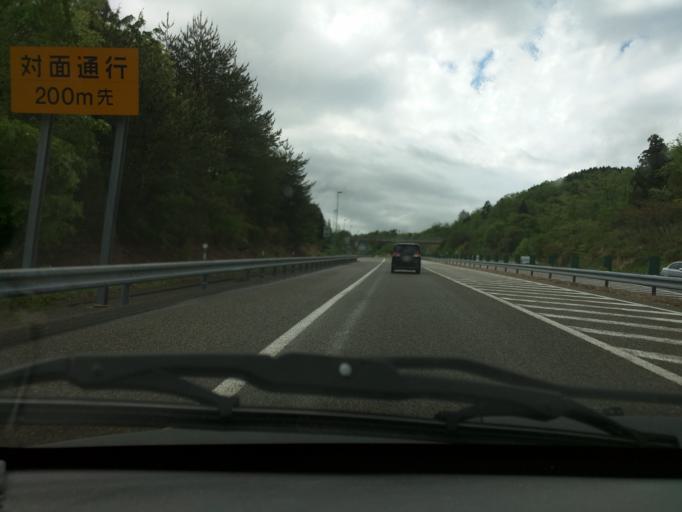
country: JP
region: Niigata
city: Joetsu
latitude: 37.1272
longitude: 138.2128
